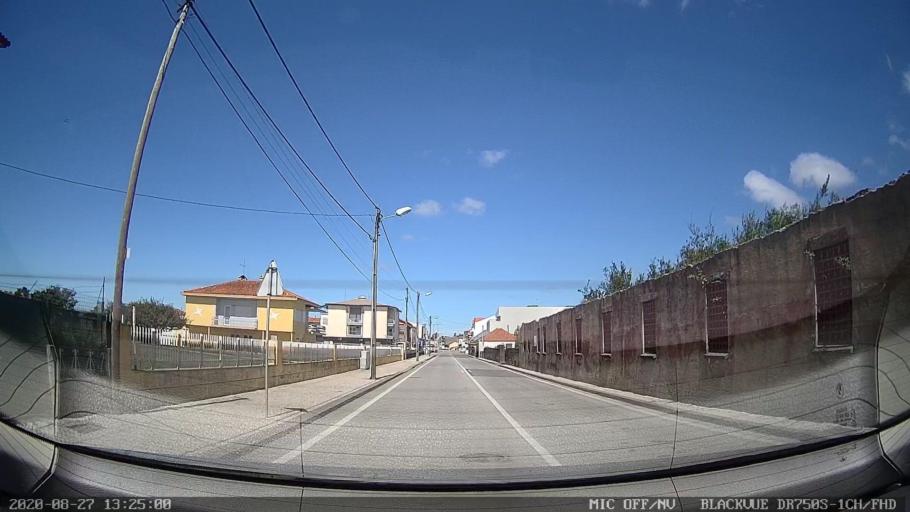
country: PT
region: Aveiro
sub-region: Vagos
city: Vagos
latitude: 40.5495
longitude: -8.6796
